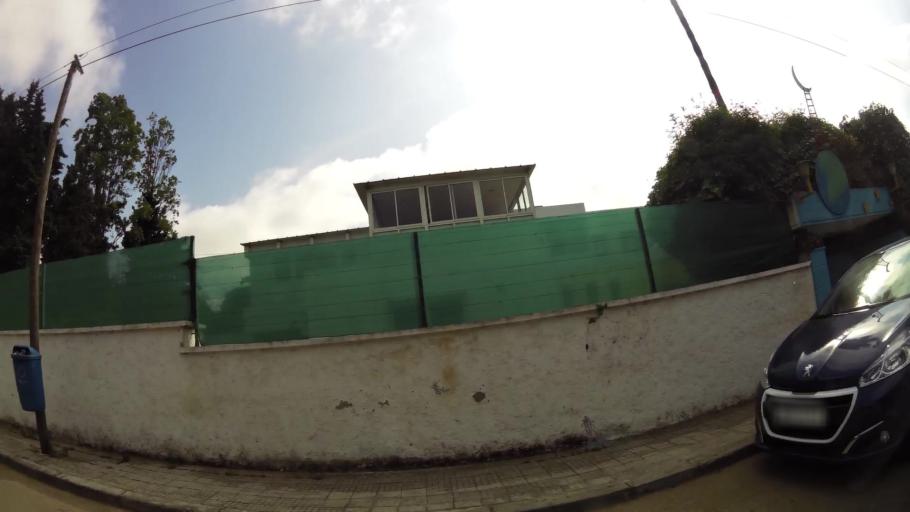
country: MA
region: Rabat-Sale-Zemmour-Zaer
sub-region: Rabat
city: Rabat
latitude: 33.9732
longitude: -6.8466
